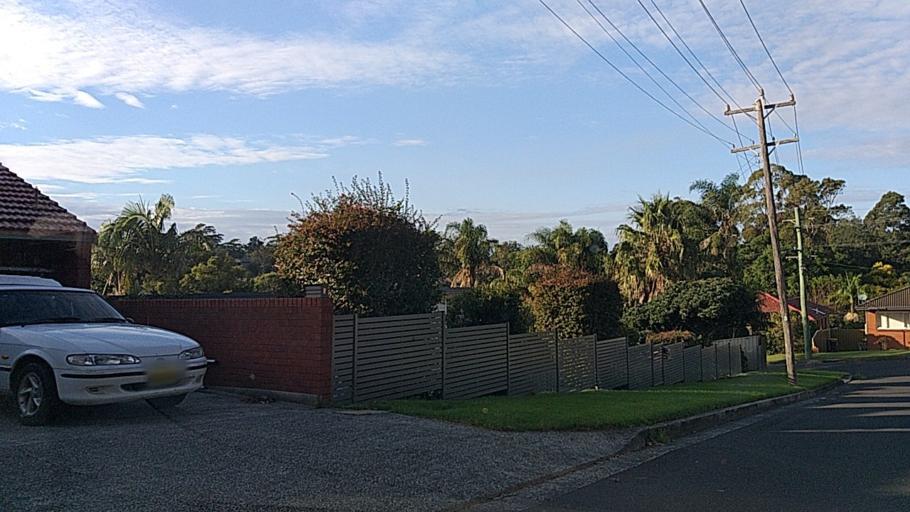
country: AU
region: New South Wales
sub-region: Wollongong
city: Mount Ousley
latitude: -34.3977
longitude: 150.8779
